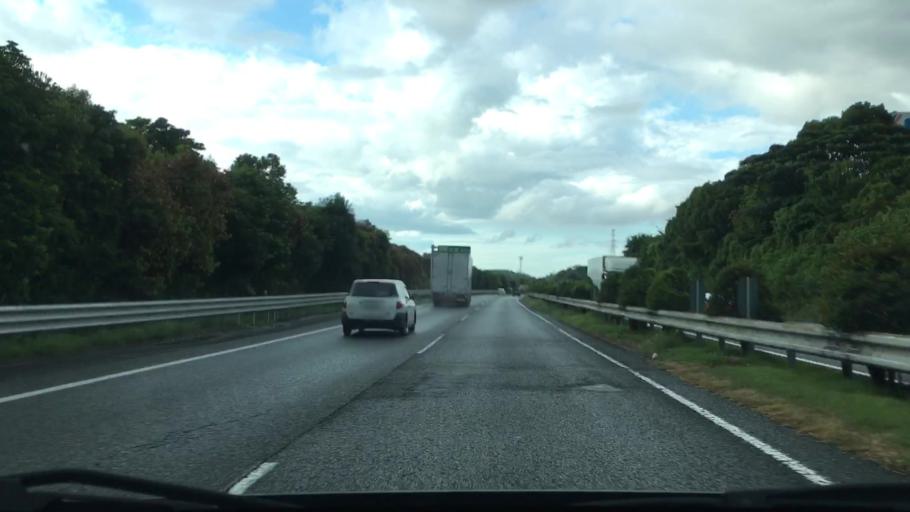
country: JP
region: Fukuoka
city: Koga
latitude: 33.6999
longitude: 130.4853
